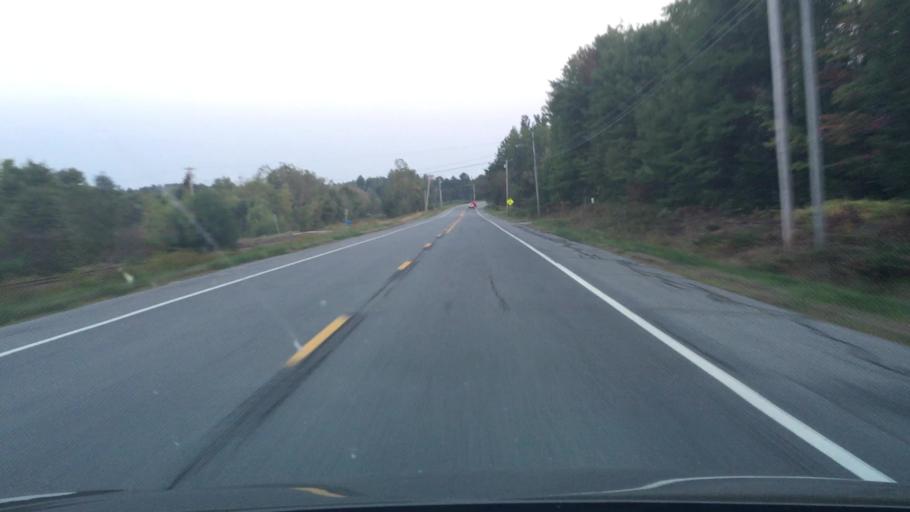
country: US
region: Maine
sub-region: Waldo County
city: Stockton Springs
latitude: 44.5420
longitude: -68.8626
